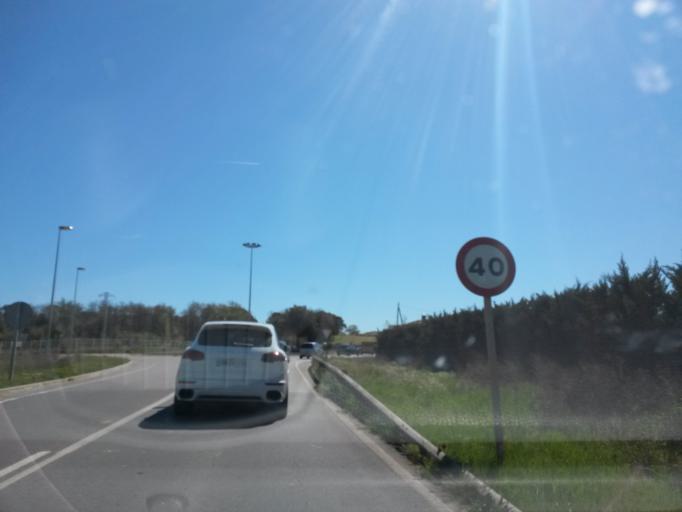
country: ES
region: Catalonia
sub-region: Provincia de Girona
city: Riudellots de la Selva
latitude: 41.8976
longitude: 2.8227
